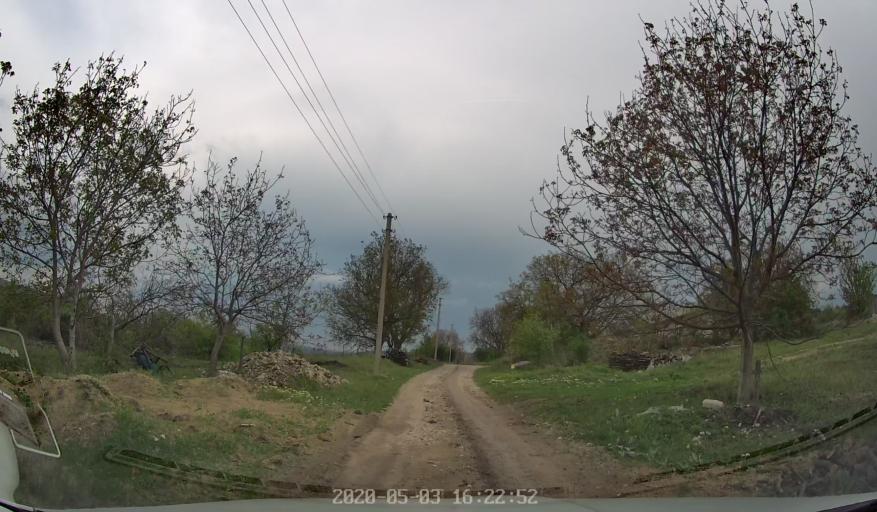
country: MD
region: Calarasi
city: Calarasi
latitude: 47.1987
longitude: 28.3476
